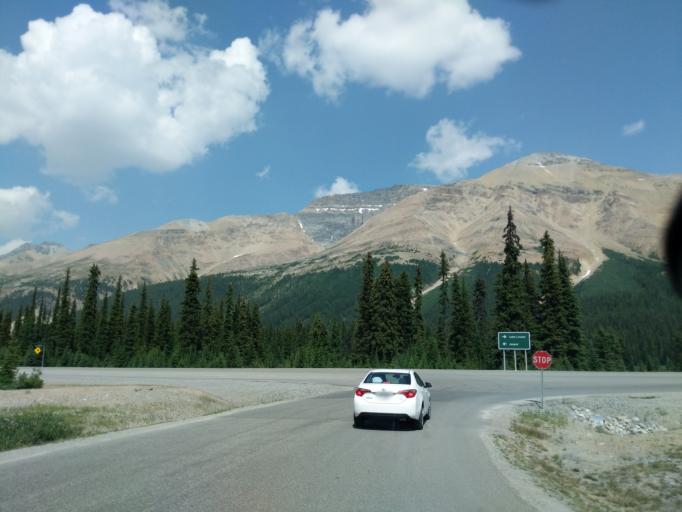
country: CA
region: Alberta
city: Lake Louise
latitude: 51.7197
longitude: -116.4949
